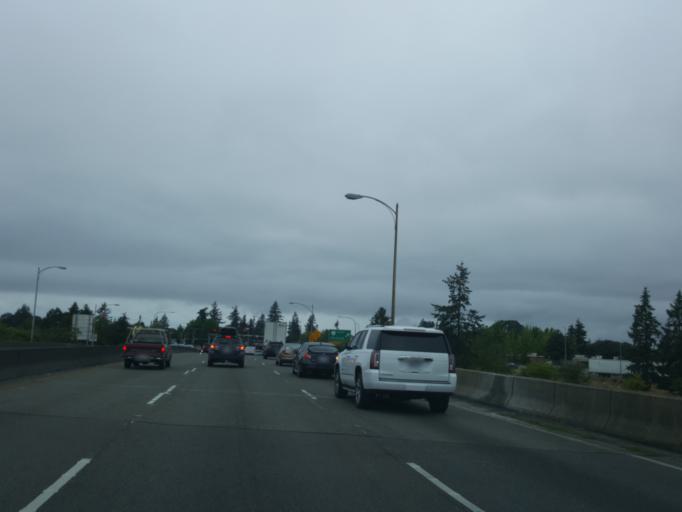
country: US
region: Washington
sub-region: Pierce County
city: McChord Air Force Base
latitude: 47.1629
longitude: -122.4788
